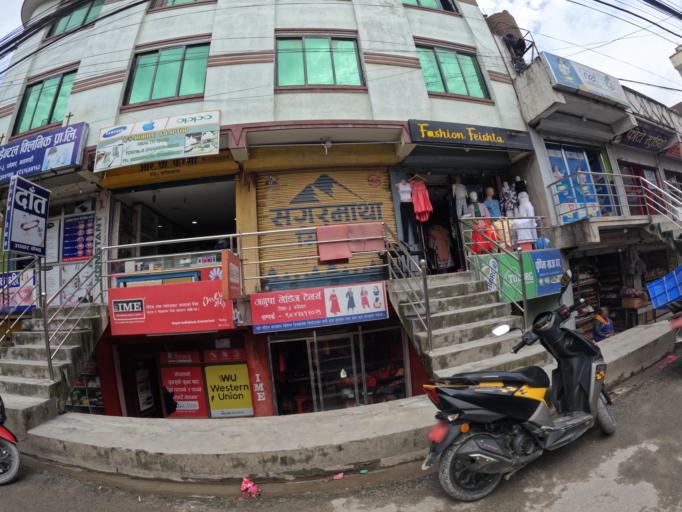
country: NP
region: Central Region
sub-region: Bagmati Zone
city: Kathmandu
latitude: 27.7532
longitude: 85.3181
